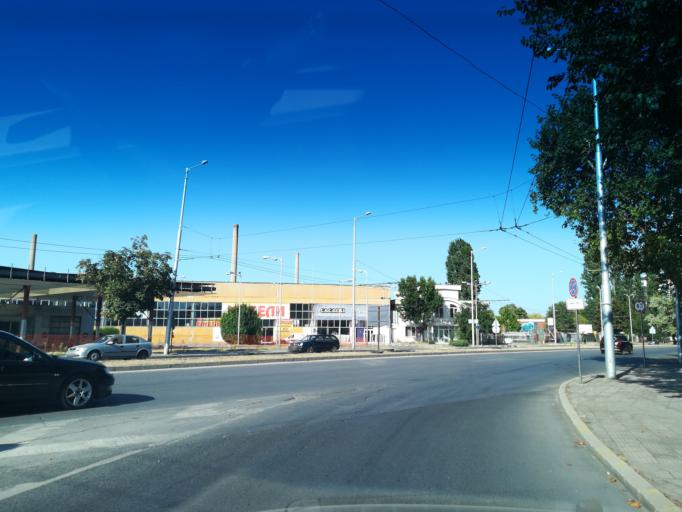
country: BG
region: Plovdiv
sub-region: Obshtina Plovdiv
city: Plovdiv
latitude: 42.1614
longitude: 24.7302
